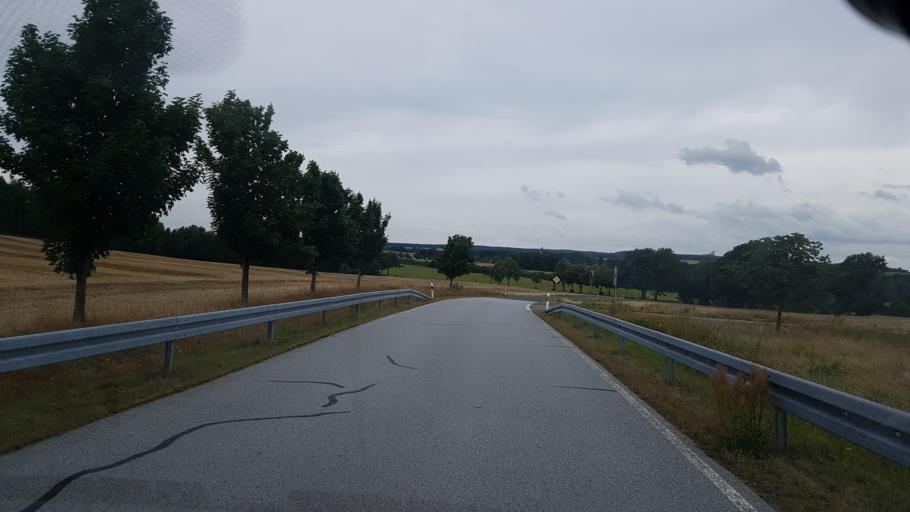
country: DE
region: Saxony
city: Reichenbach
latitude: 51.2131
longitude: 14.7994
